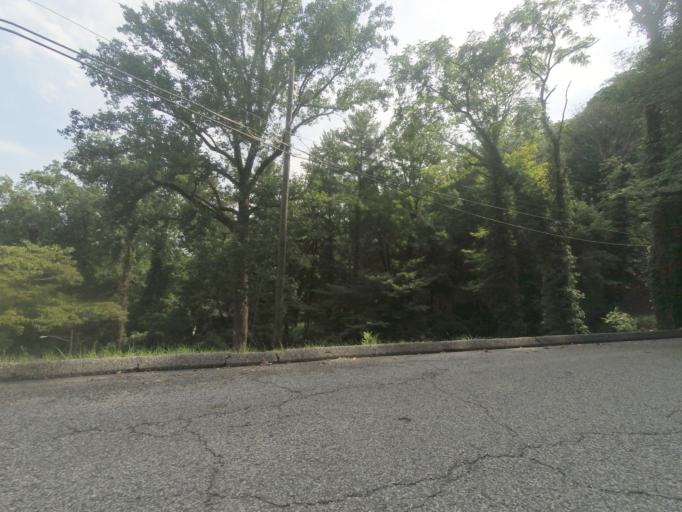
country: US
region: West Virginia
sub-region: Cabell County
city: Huntington
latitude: 38.4031
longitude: -82.4585
